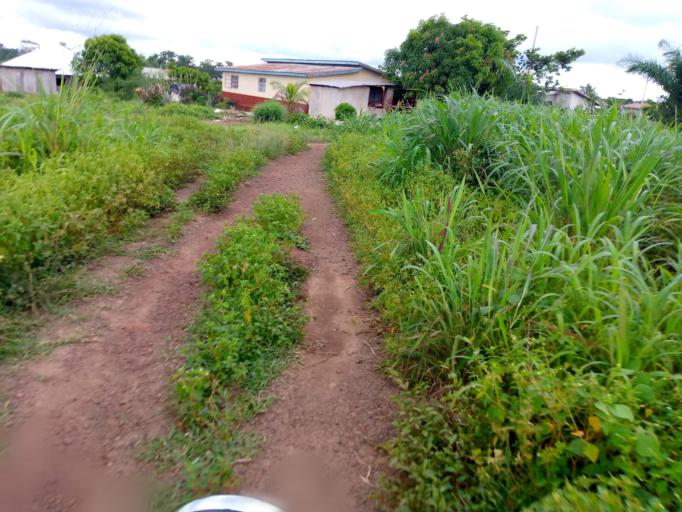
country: SL
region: Southern Province
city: Moyamba
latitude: 8.1532
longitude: -12.4405
